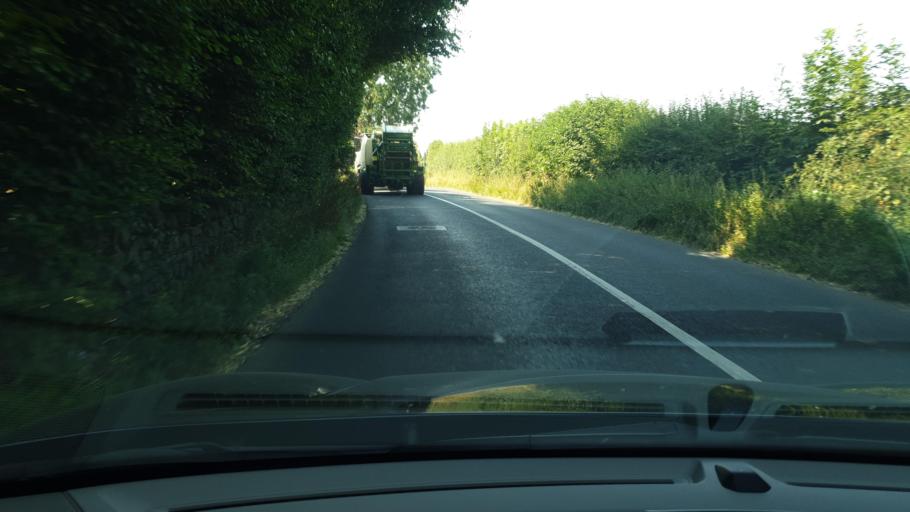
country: IE
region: Leinster
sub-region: An Mhi
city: Athboy
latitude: 53.6187
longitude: -6.9088
